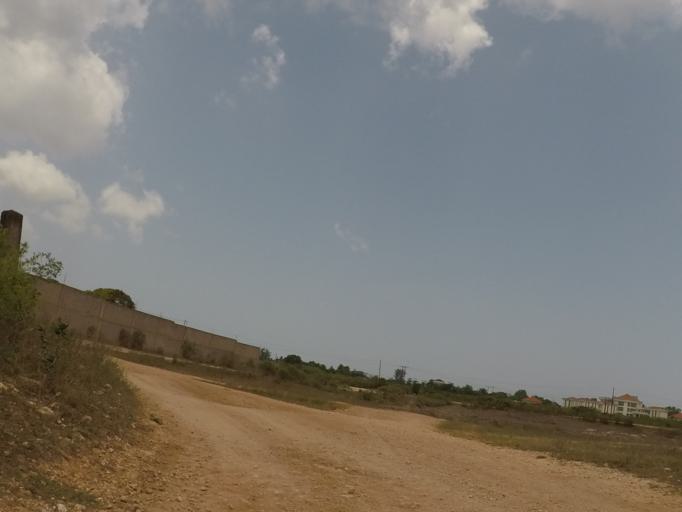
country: TZ
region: Zanzibar Central/South
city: Koani
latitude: -6.1930
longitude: 39.3094
